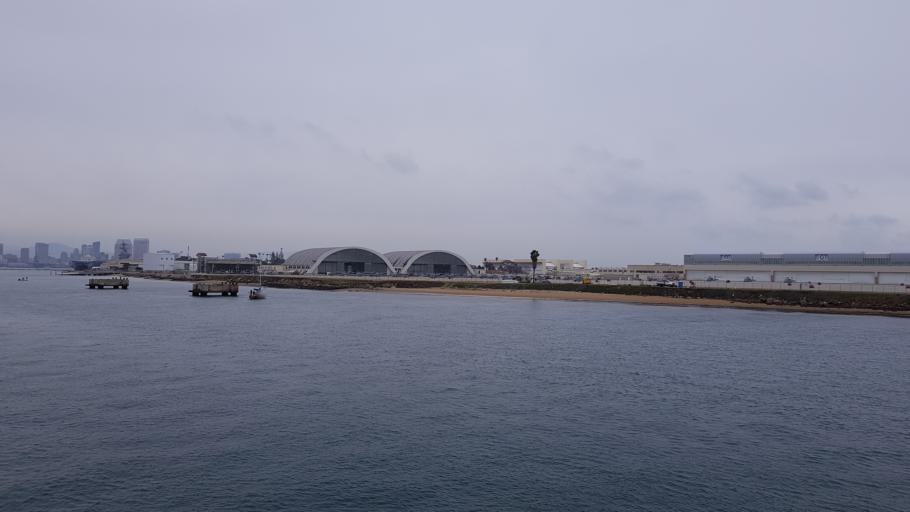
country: US
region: California
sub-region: San Diego County
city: Coronado
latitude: 32.7157
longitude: -117.2075
